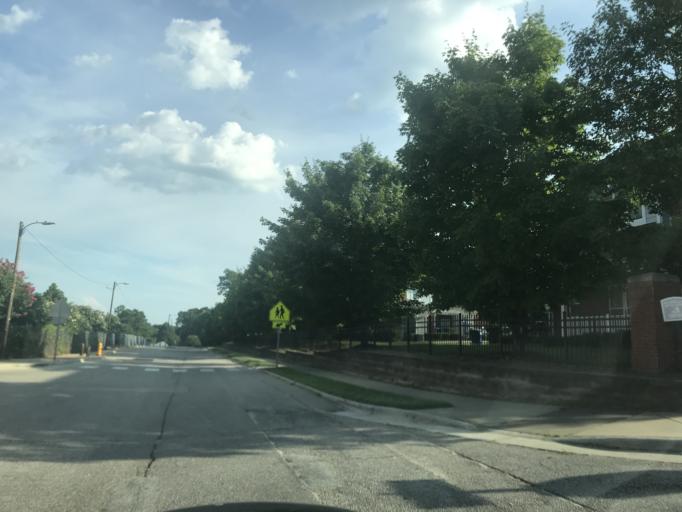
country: US
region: North Carolina
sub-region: Wake County
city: Raleigh
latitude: 35.7707
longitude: -78.6270
